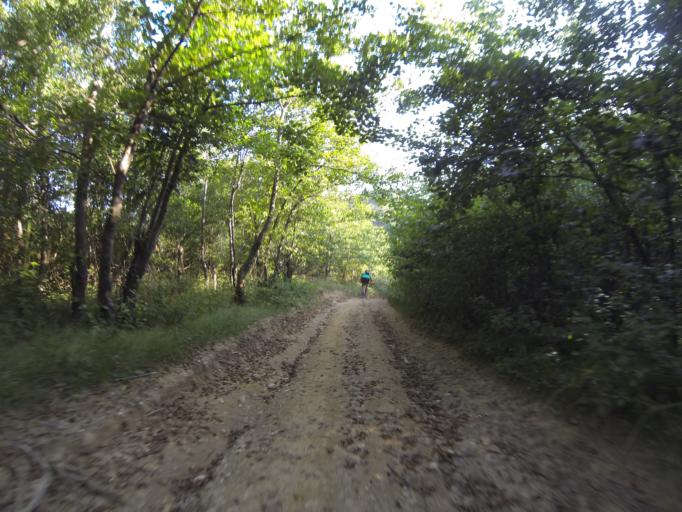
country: RO
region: Valcea
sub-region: Comuna Costesti
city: Bistrita
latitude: 45.1978
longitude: 23.9840
